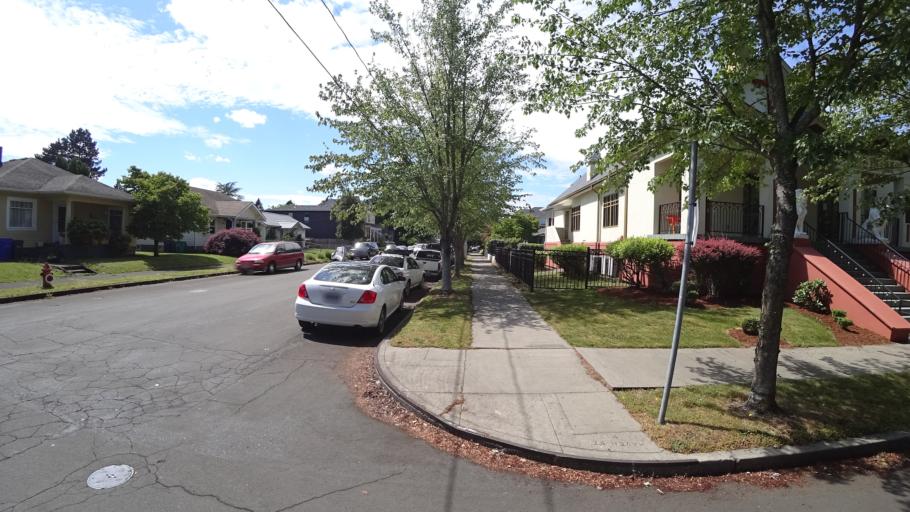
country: US
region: Oregon
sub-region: Multnomah County
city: Portland
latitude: 45.5803
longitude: -122.7206
